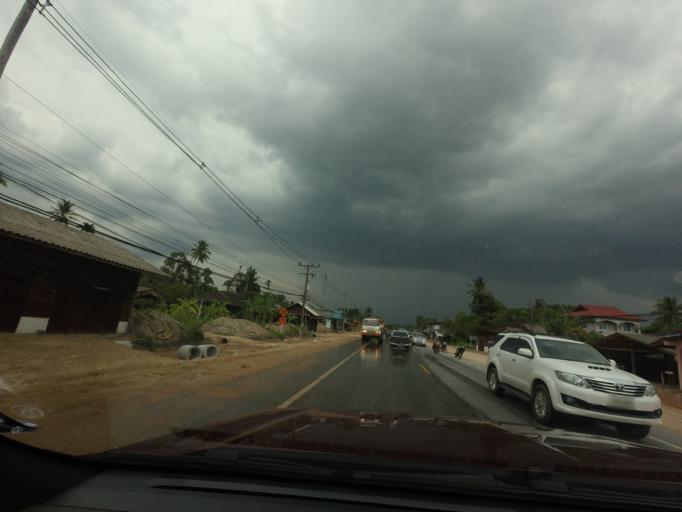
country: TH
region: Yala
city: Krong Pi Nang
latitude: 6.4312
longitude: 101.2784
